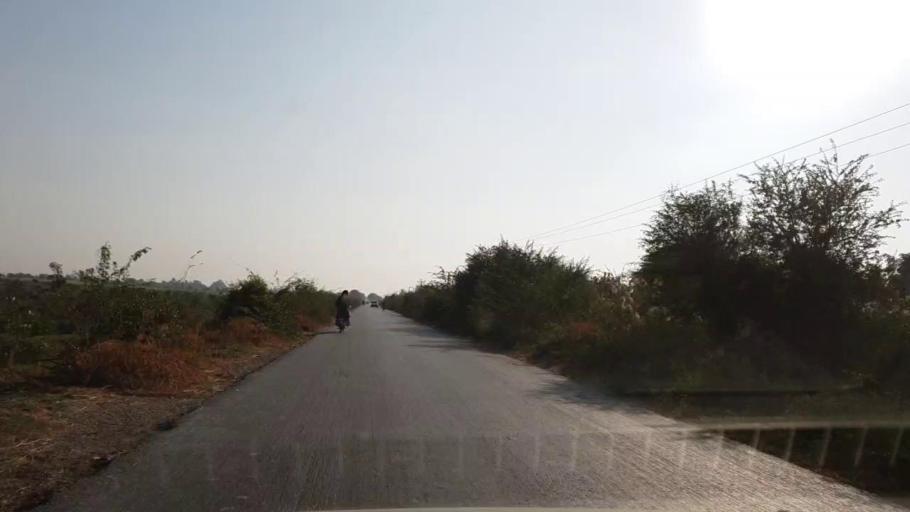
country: PK
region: Sindh
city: Bulri
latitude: 24.8831
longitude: 68.3418
